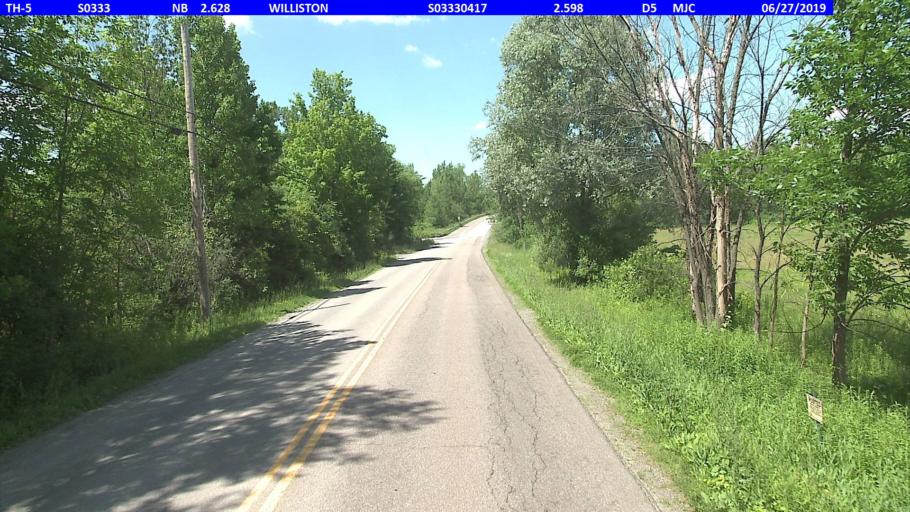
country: US
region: Vermont
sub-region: Chittenden County
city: South Burlington
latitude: 44.4384
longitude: -73.1314
